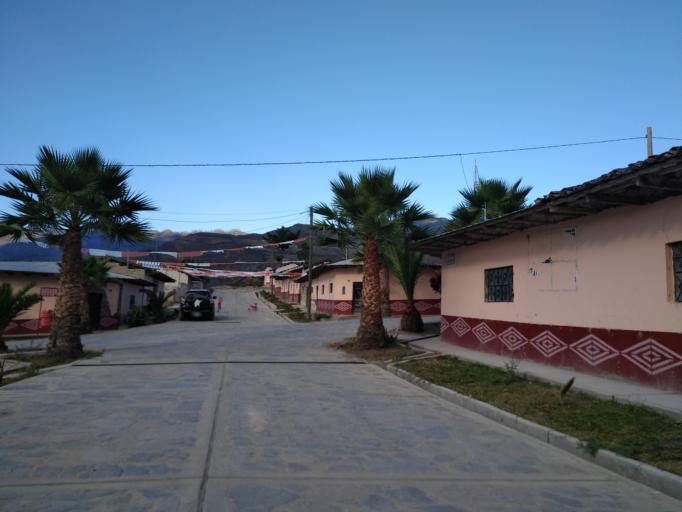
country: PE
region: Amazonas
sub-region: Provincia de Luya
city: Tingo
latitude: -6.3718
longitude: -77.9103
